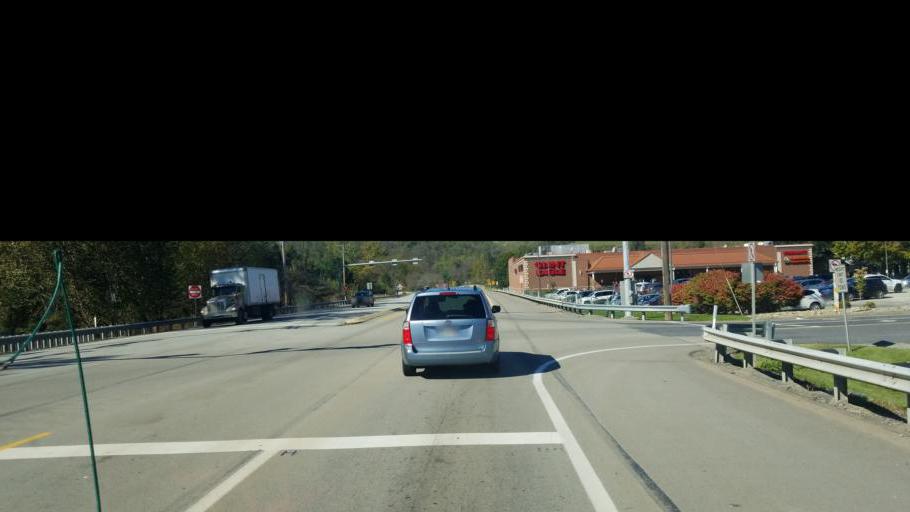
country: US
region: Pennsylvania
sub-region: Westmoreland County
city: Ligonier
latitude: 40.2455
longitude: -79.2445
